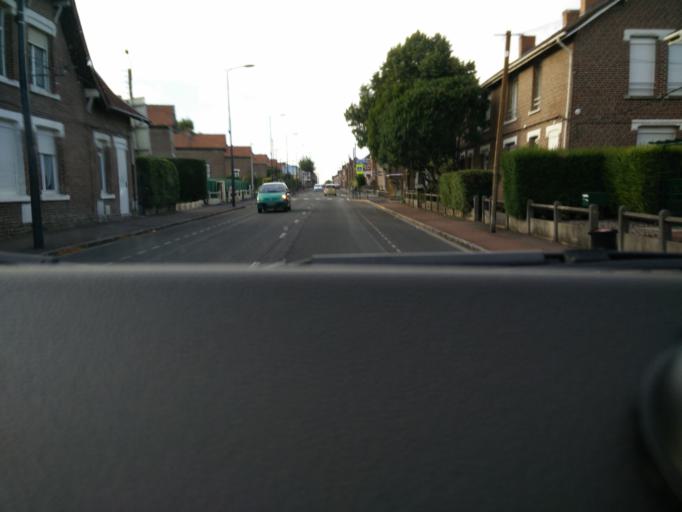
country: FR
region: Nord-Pas-de-Calais
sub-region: Departement du Pas-de-Calais
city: Lens
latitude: 50.4433
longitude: 2.8199
